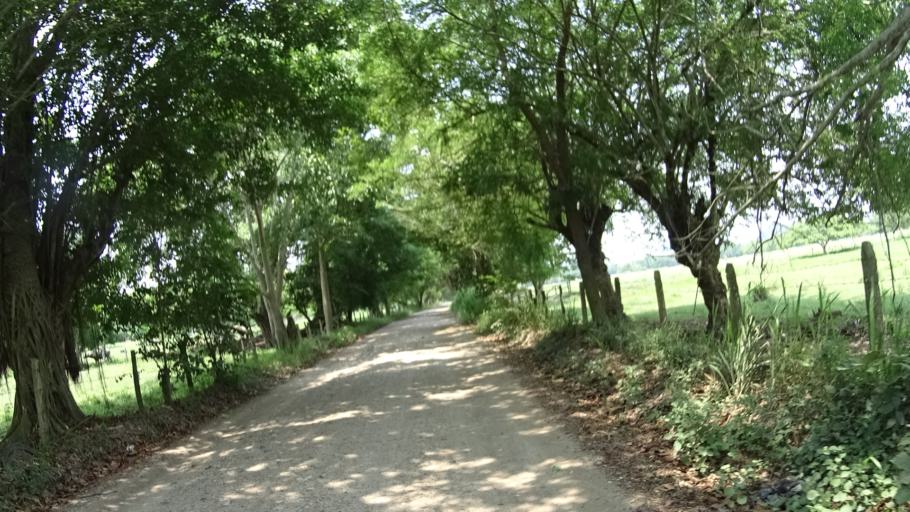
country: CO
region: Cundinamarca
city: Puerto Salgar
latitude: 5.5170
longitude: -74.6879
